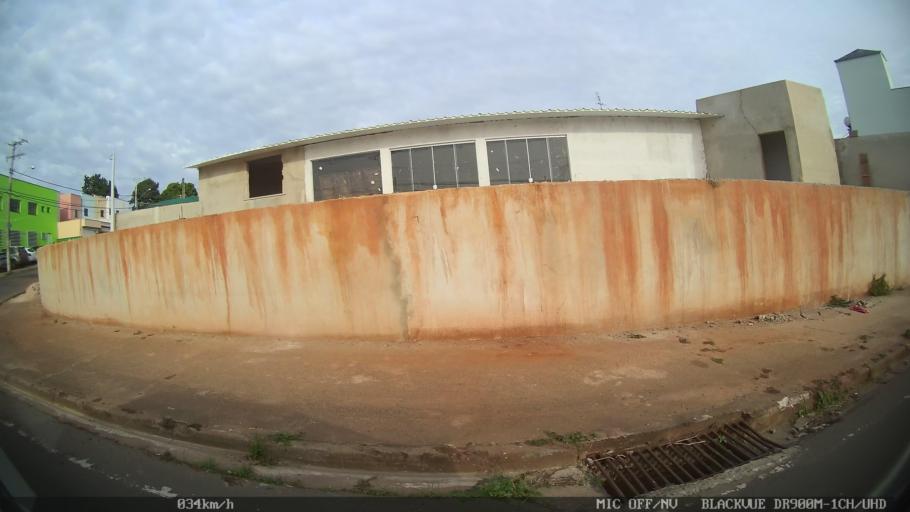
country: BR
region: Sao Paulo
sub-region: Piracicaba
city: Piracicaba
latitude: -22.7421
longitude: -47.6126
